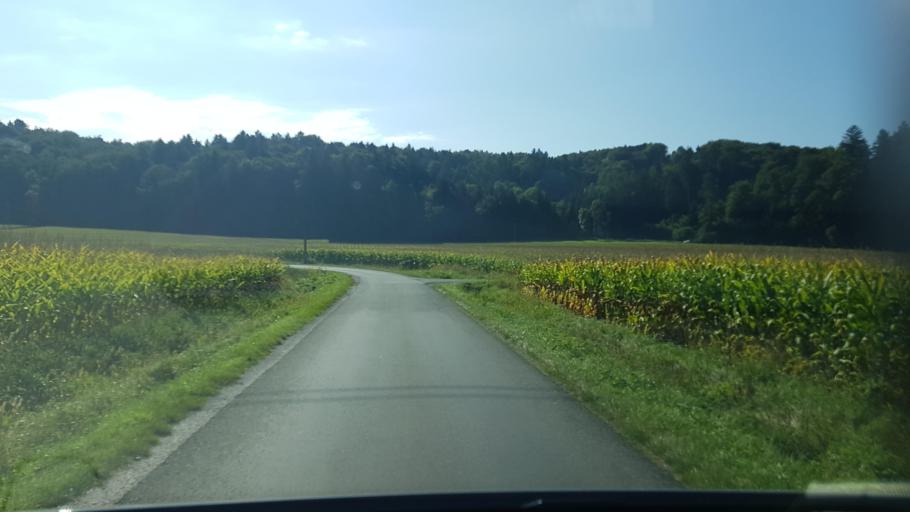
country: AT
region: Styria
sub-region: Politischer Bezirk Deutschlandsberg
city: Wettmannstatten
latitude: 46.8240
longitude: 15.3559
